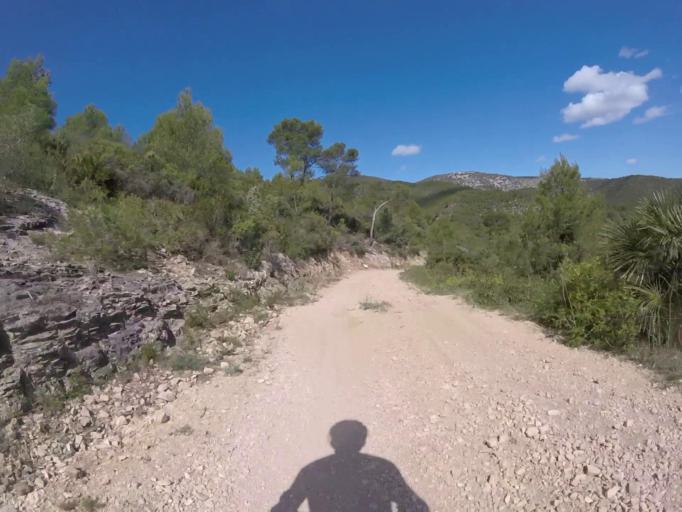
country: ES
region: Valencia
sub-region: Provincia de Castello
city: Santa Magdalena de Pulpis
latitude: 40.3083
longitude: 0.3214
